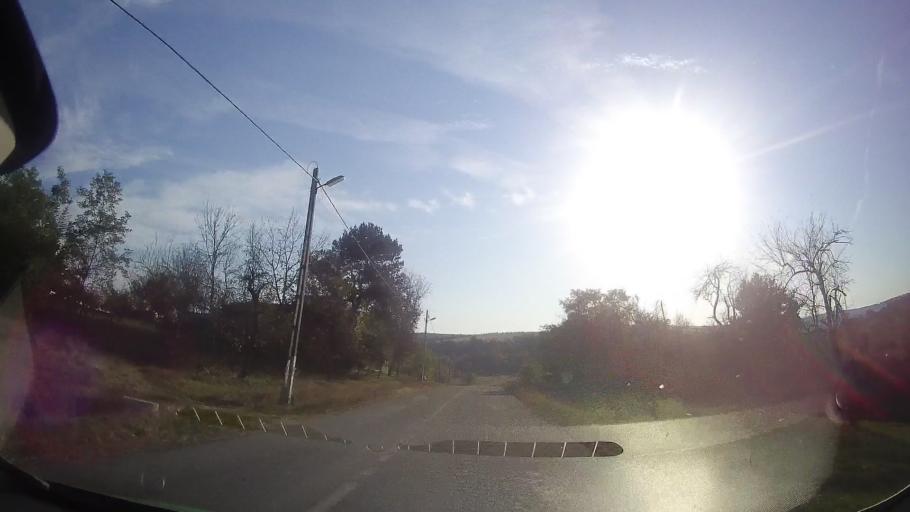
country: RO
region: Timis
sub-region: Comuna Bogda
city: Bogda
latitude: 45.9740
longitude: 21.5975
